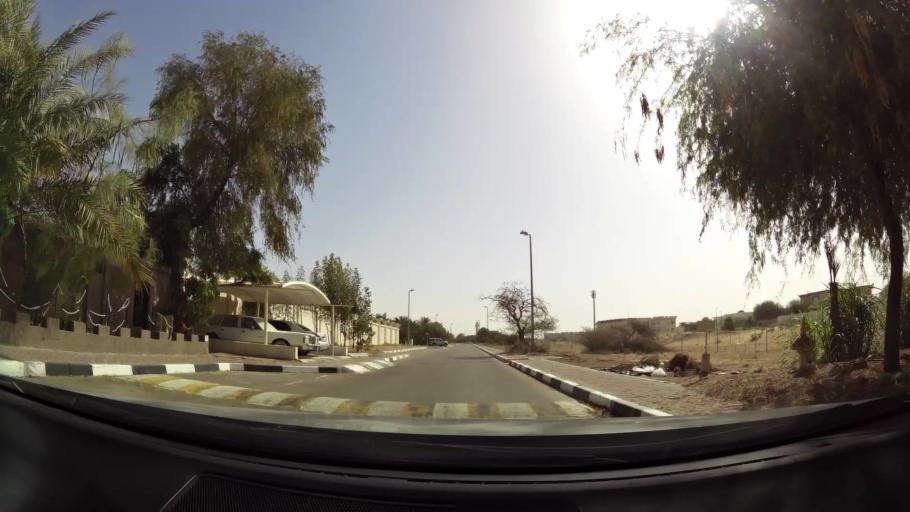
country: OM
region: Al Buraimi
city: Al Buraymi
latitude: 24.3278
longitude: 55.7944
